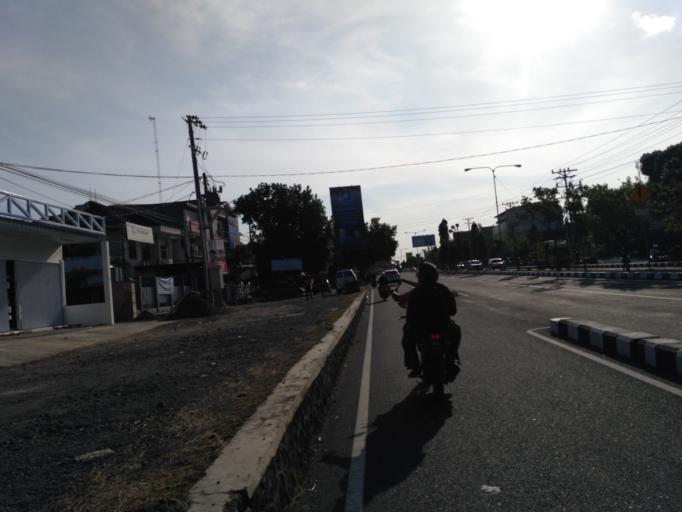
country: ID
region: Daerah Istimewa Yogyakarta
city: Depok
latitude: -7.7627
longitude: 110.4159
